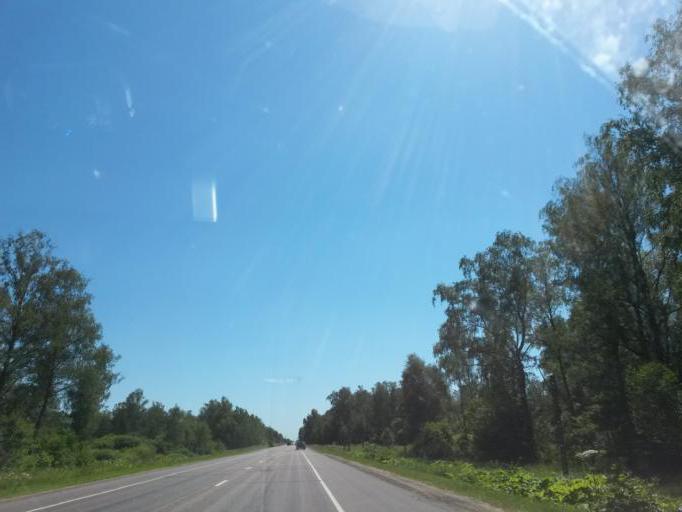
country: RU
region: Moskovskaya
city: Proletarskiy
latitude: 55.0535
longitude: 37.4334
